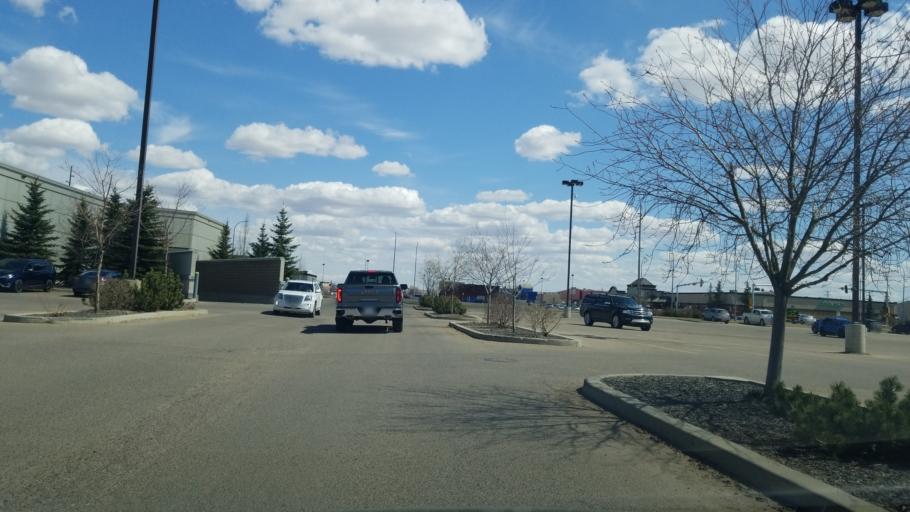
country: CA
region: Saskatchewan
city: Lloydminster
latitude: 53.2770
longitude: -110.0564
